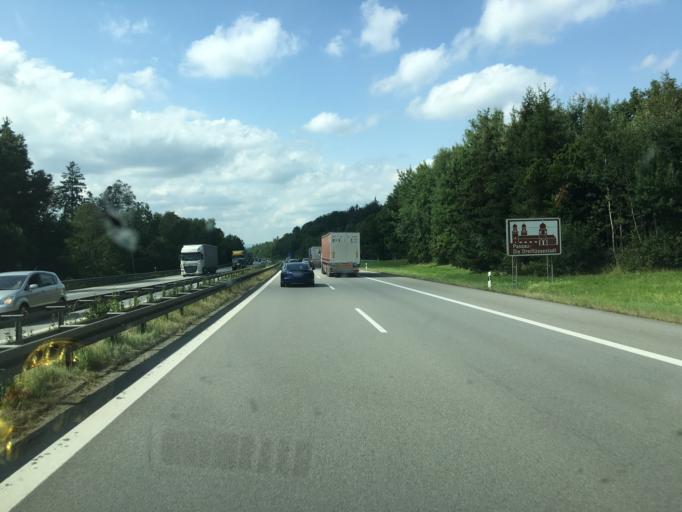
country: DE
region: Bavaria
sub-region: Lower Bavaria
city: Passau
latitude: 48.5451
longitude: 13.3981
